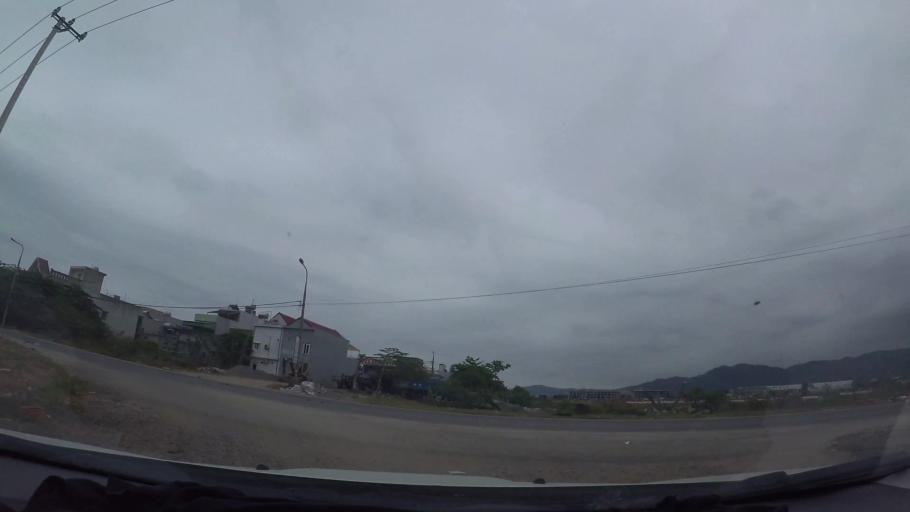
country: VN
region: Da Nang
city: Lien Chieu
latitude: 16.1026
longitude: 108.1301
